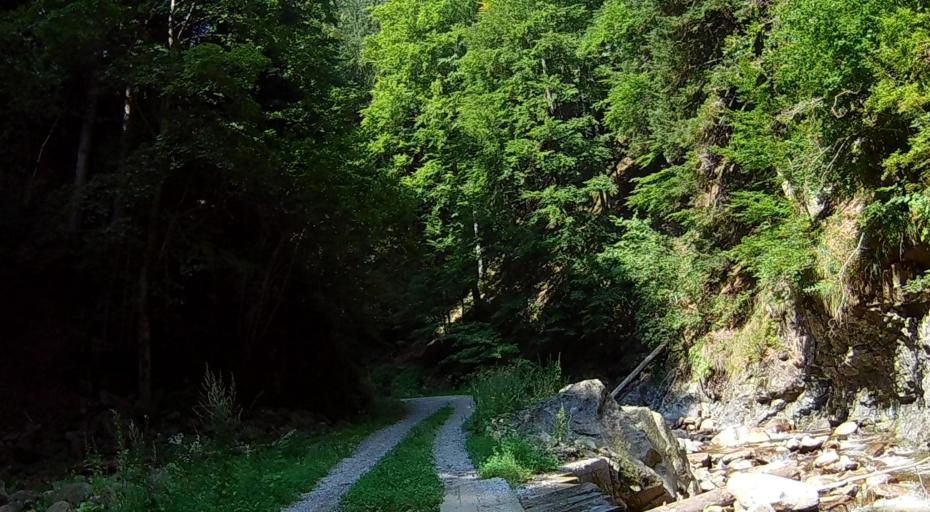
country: SI
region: Selnica ob Dravi
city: Selnica ob Dravi
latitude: 46.5054
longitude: 15.4560
